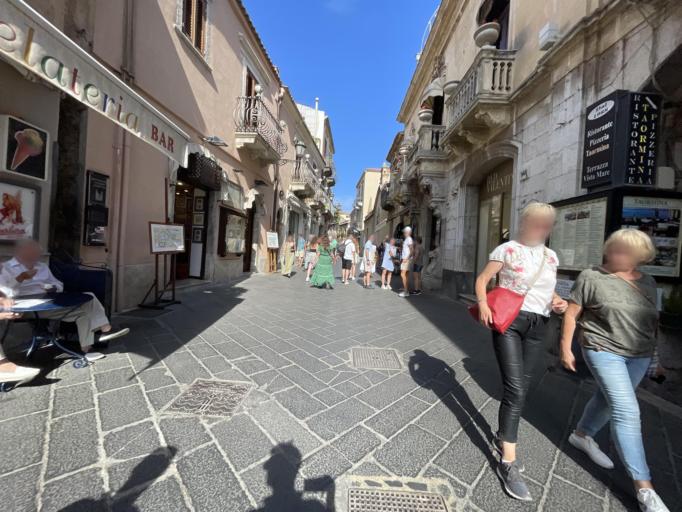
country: IT
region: Sicily
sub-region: Messina
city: Taormina
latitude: 37.8519
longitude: 15.2862
